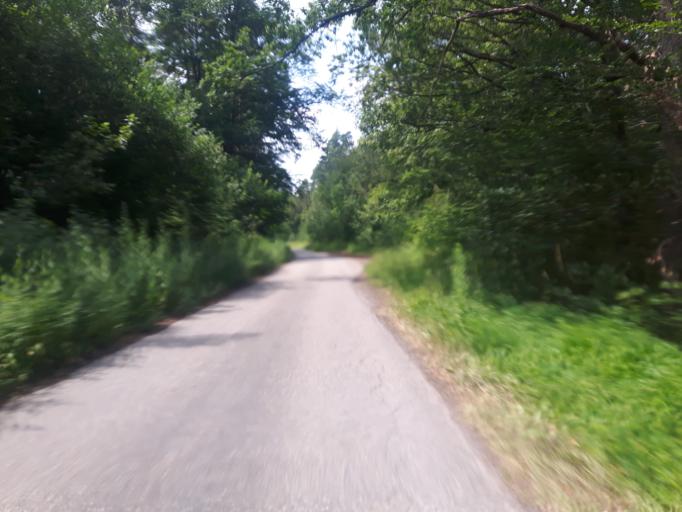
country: DE
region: Baden-Wuerttemberg
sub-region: Regierungsbezirk Stuttgart
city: Pfaffenhofen
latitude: 49.0376
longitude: 8.9891
